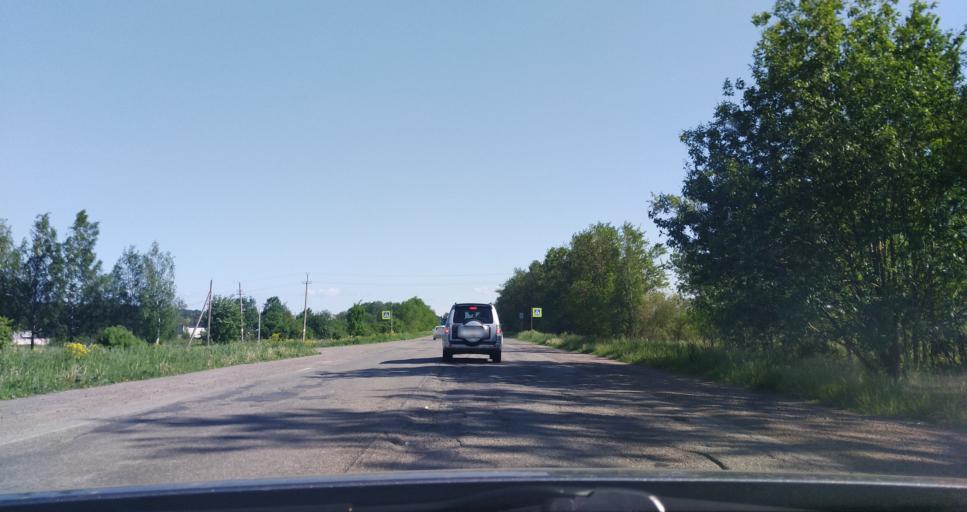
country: RU
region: St.-Petersburg
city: Krasnoye Selo
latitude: 59.7040
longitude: 30.0946
